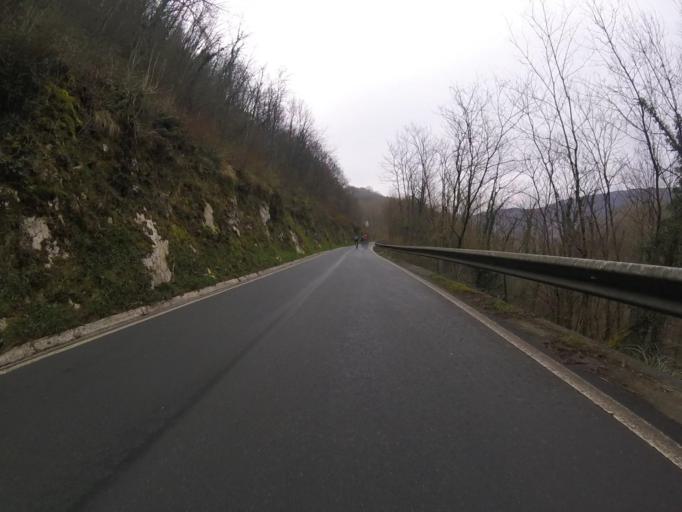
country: ES
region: Navarre
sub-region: Provincia de Navarra
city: Arantza
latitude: 43.2043
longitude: -1.7133
